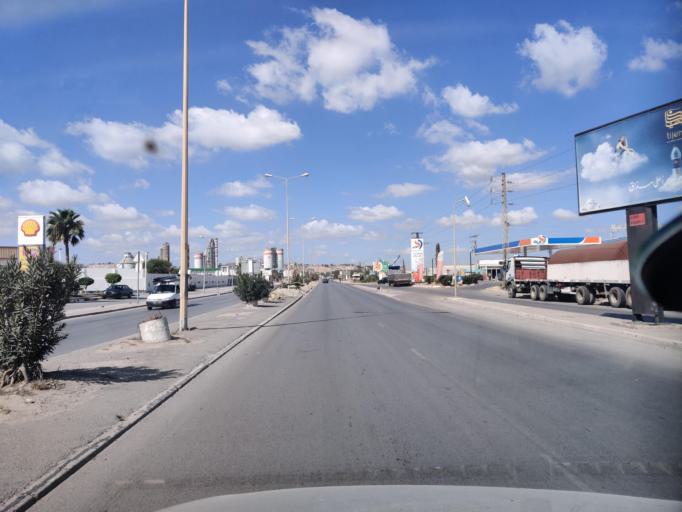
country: TN
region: Bin 'Arus
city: Ben Arous
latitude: 36.7758
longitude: 10.2137
